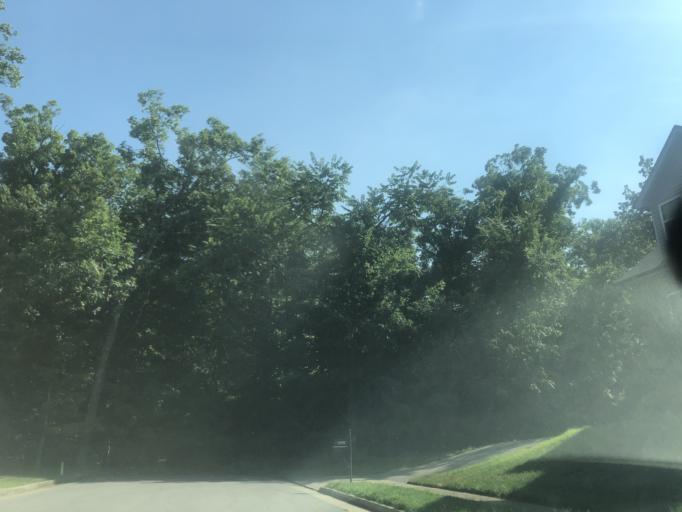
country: US
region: Tennessee
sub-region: Wilson County
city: Green Hill
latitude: 36.1413
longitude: -86.5912
